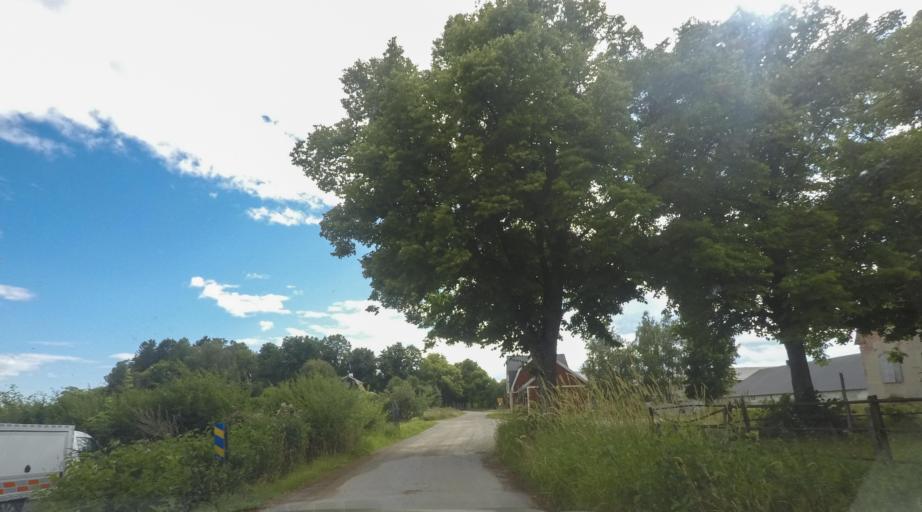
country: SE
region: Stockholm
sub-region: Sodertalje Kommun
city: Pershagen
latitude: 59.1135
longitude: 17.6593
